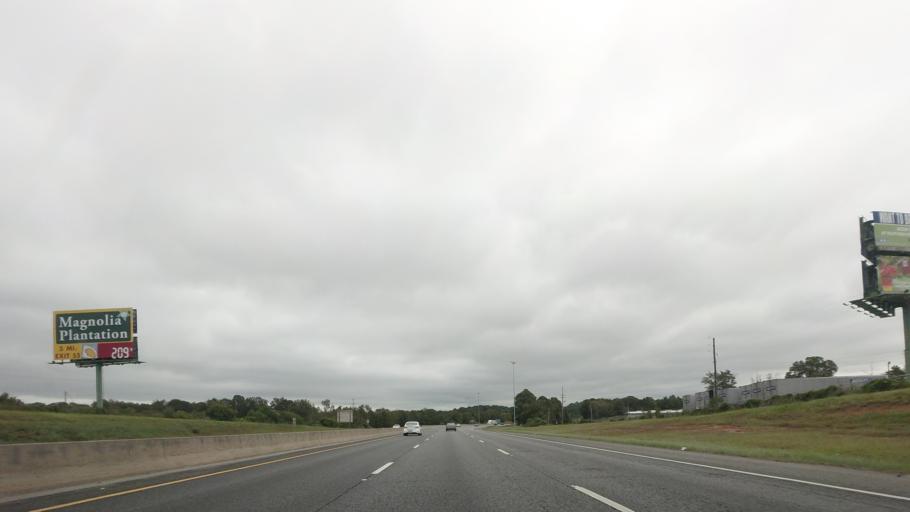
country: US
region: Georgia
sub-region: Tift County
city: Unionville
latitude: 31.4235
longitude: -83.5093
